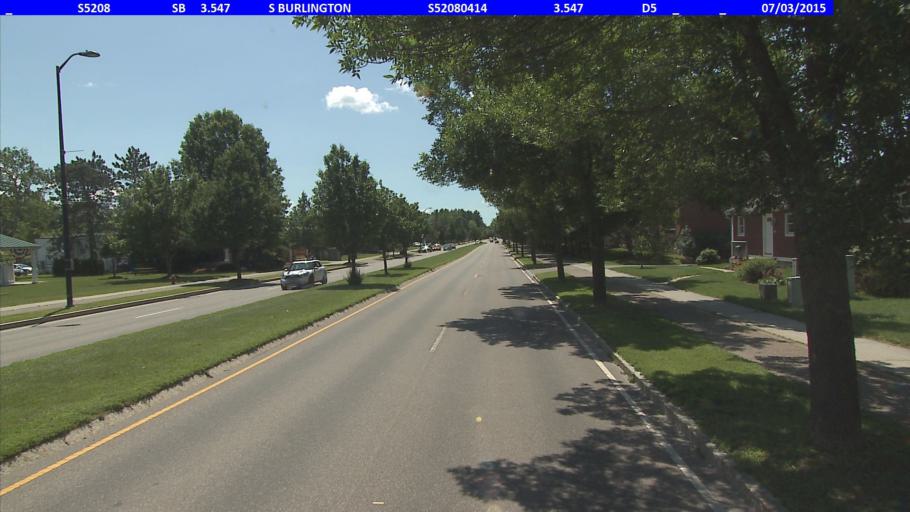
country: US
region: Vermont
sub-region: Chittenden County
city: South Burlington
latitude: 44.4612
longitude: -73.1803
